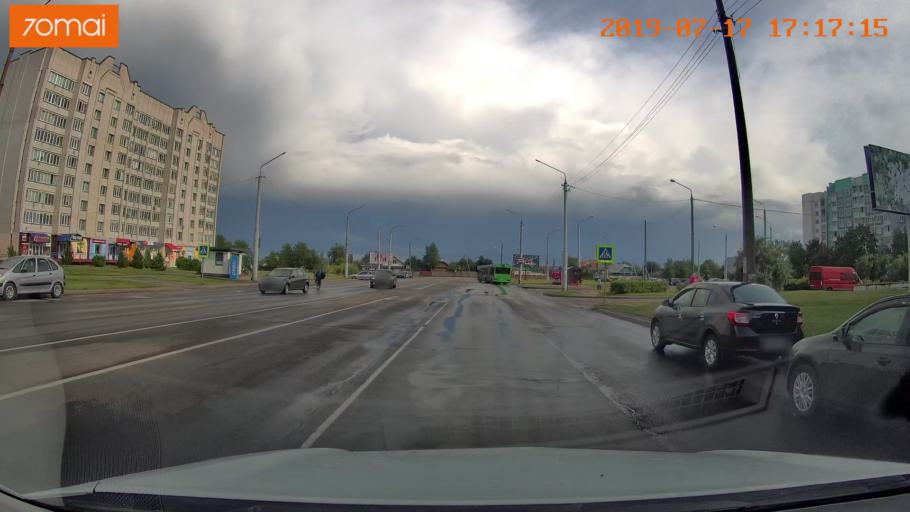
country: BY
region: Mogilev
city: Babruysk
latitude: 53.1616
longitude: 29.1985
